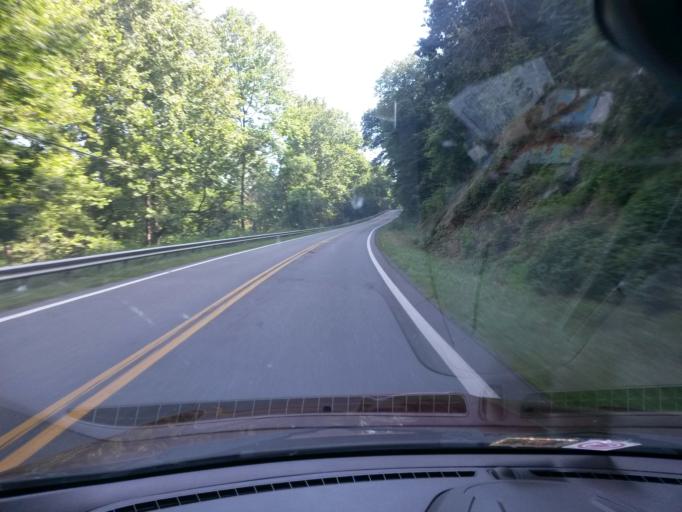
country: US
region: Virginia
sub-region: Rockingham County
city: Broadway
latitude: 38.6757
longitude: -78.9291
